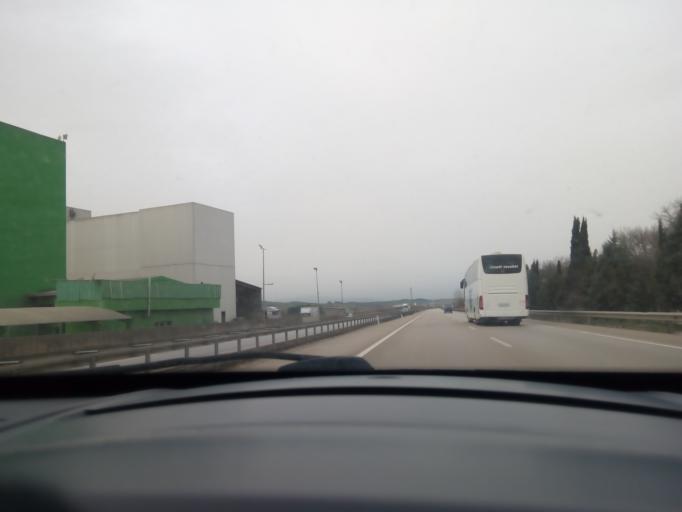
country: TR
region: Bursa
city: Tatkavakli
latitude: 40.0301
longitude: 28.3250
